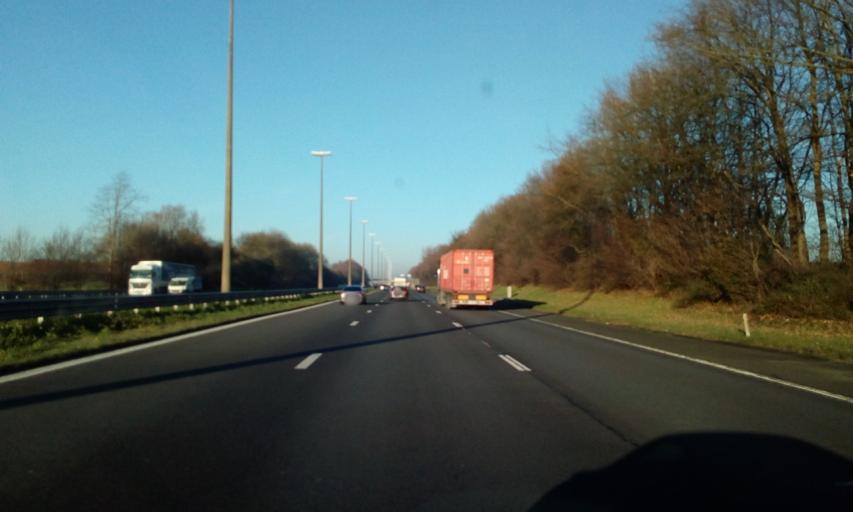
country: BE
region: Wallonia
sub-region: Province du Brabant Wallon
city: Ittre
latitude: 50.6474
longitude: 4.3088
